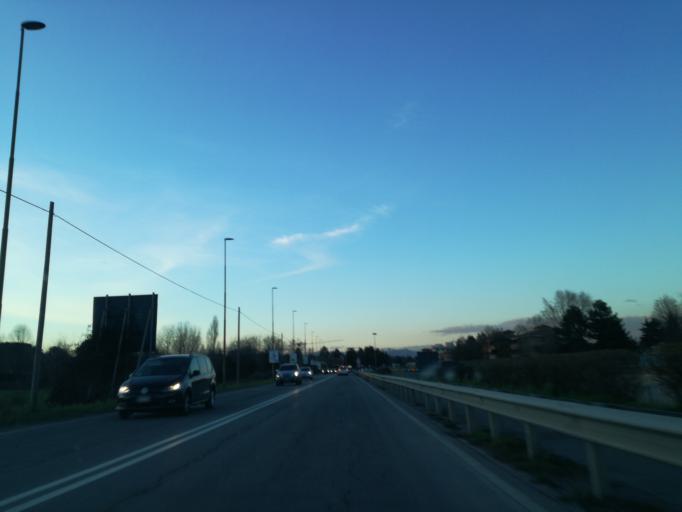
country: IT
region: Lombardy
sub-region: Provincia di Monza e Brianza
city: Vimercate
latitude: 45.6093
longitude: 9.3604
